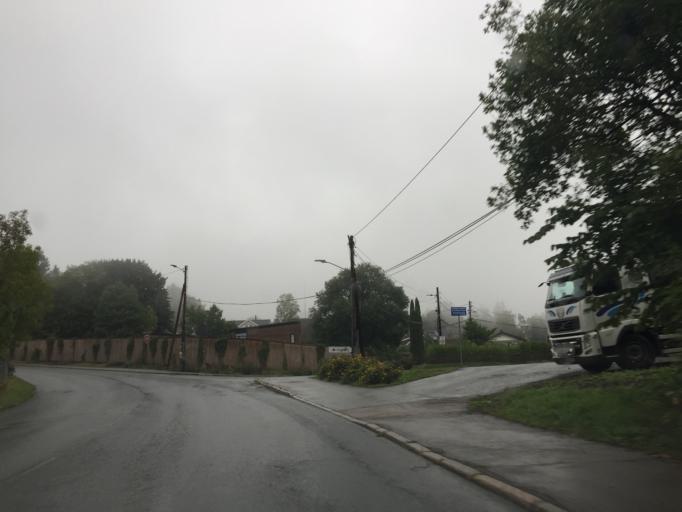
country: NO
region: Oslo
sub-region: Oslo
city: Sjolyststranda
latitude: 59.9585
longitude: 10.6898
